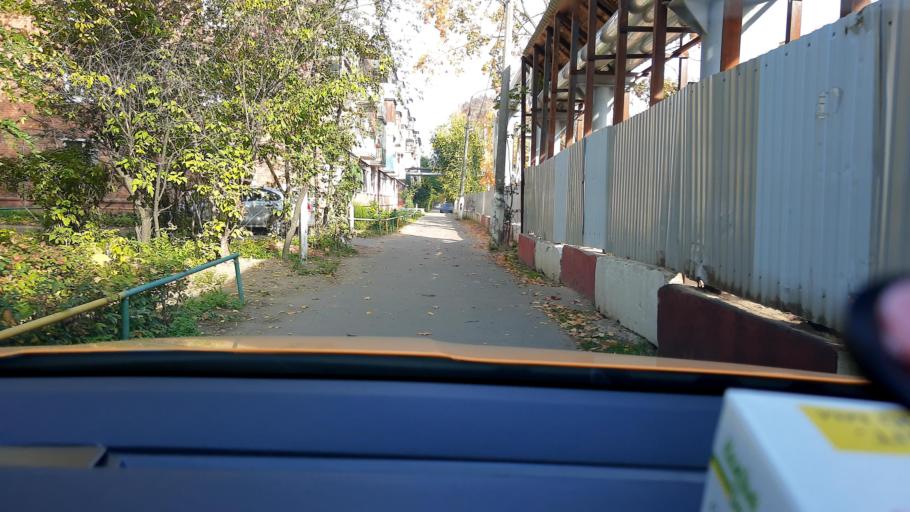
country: RU
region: Moskovskaya
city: Kotel'niki
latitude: 55.6625
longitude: 37.8530
